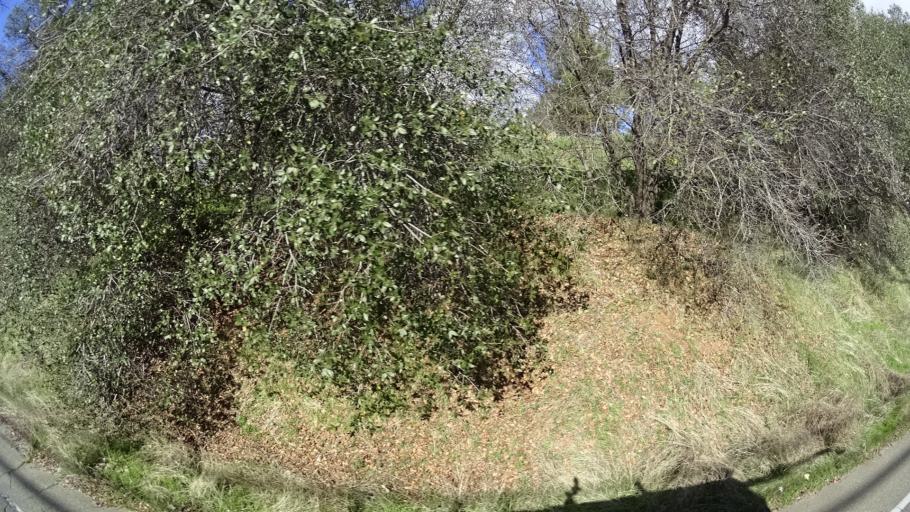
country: US
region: California
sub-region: Butte County
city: Oroville East
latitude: 39.5092
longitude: -121.5136
